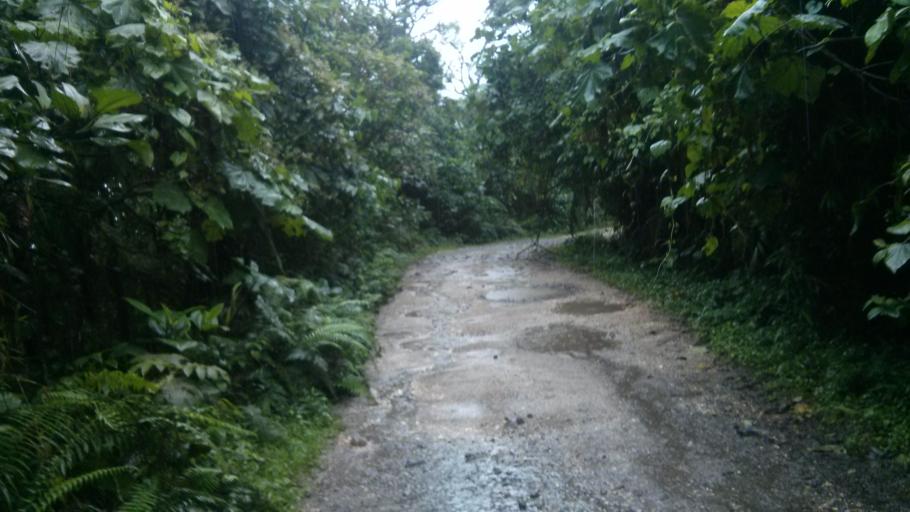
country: CR
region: San Jose
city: Ipis
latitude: 10.0308
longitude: -83.9425
